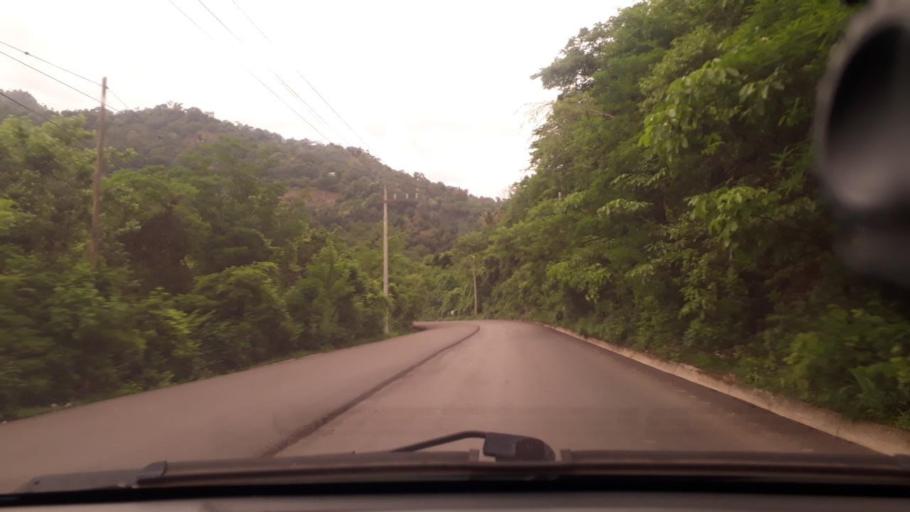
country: GT
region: Chiquimula
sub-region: Municipio de San Juan Ermita
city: San Juan Ermita
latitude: 14.7599
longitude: -89.4383
